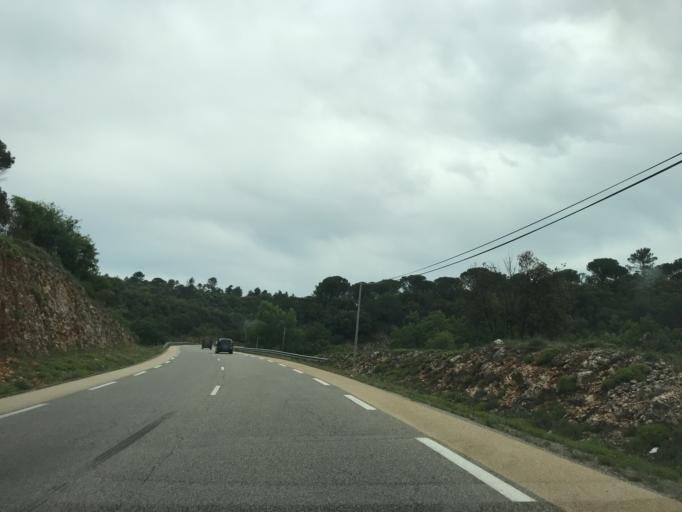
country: FR
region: Provence-Alpes-Cote d'Azur
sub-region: Departement du Var
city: Rians
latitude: 43.5879
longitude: 5.7491
